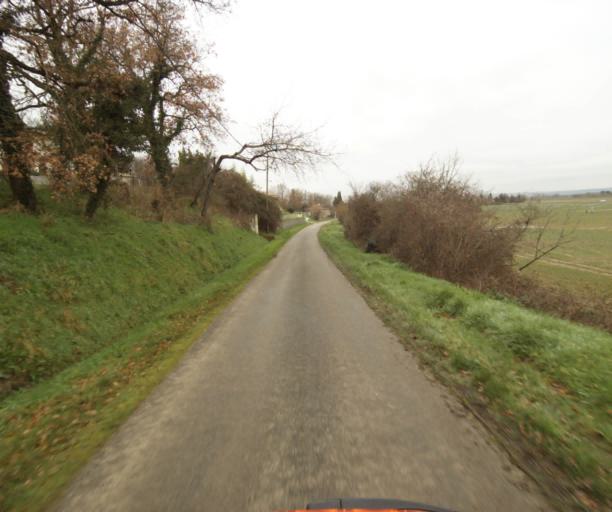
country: FR
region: Midi-Pyrenees
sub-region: Departement de l'Ariege
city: Saverdun
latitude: 43.2559
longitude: 1.5313
